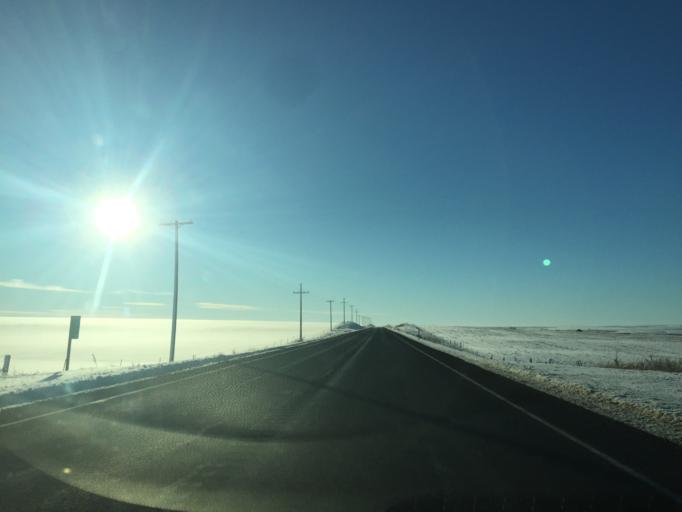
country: US
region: Washington
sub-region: Okanogan County
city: Coulee Dam
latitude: 47.7270
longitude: -118.8787
